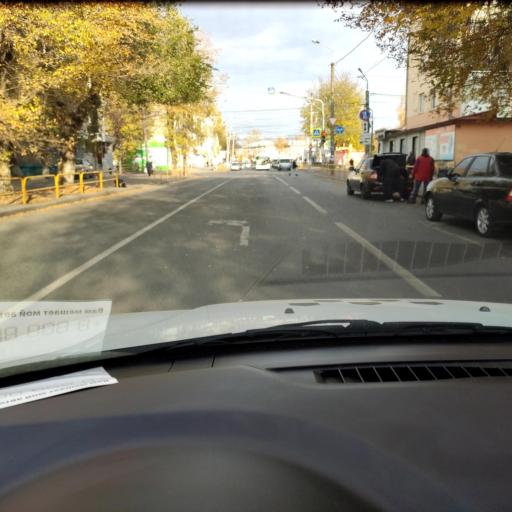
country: RU
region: Samara
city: Tol'yatti
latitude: 53.5075
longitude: 49.4160
